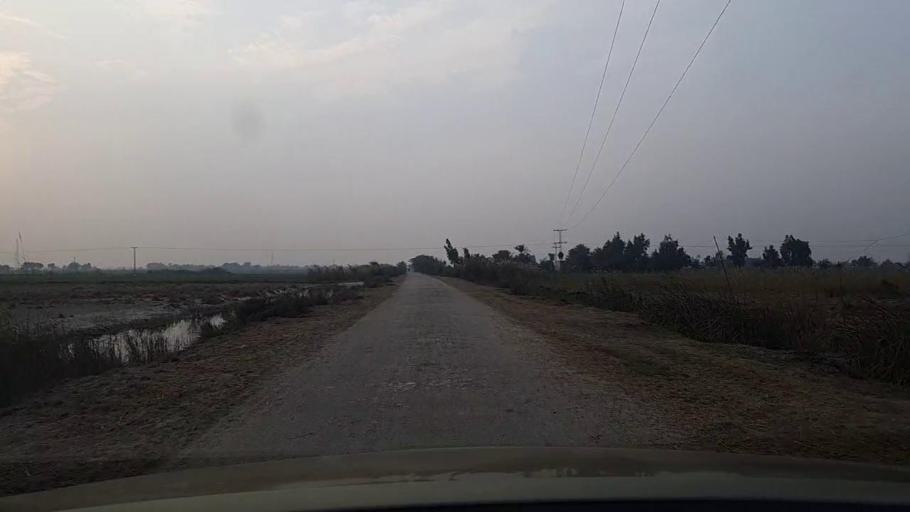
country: PK
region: Sindh
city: Sanghar
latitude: 26.1857
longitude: 68.9600
